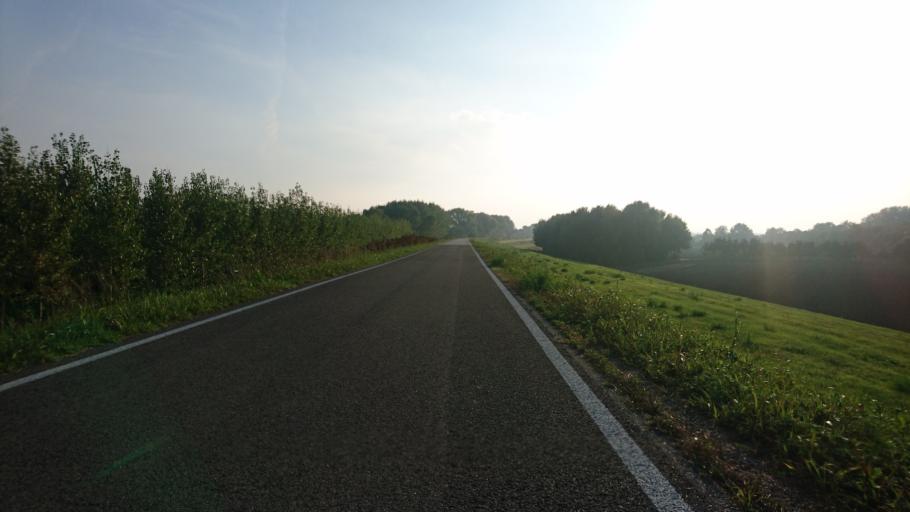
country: IT
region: Emilia-Romagna
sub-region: Provincia di Ferrara
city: Francolino
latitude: 44.9064
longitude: 11.6501
